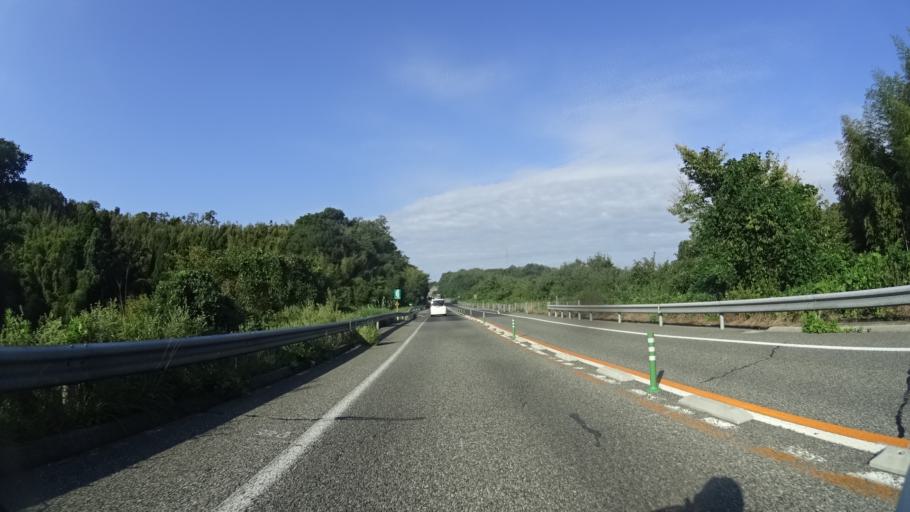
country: JP
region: Shimane
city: Matsue-shi
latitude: 35.4094
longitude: 132.9421
